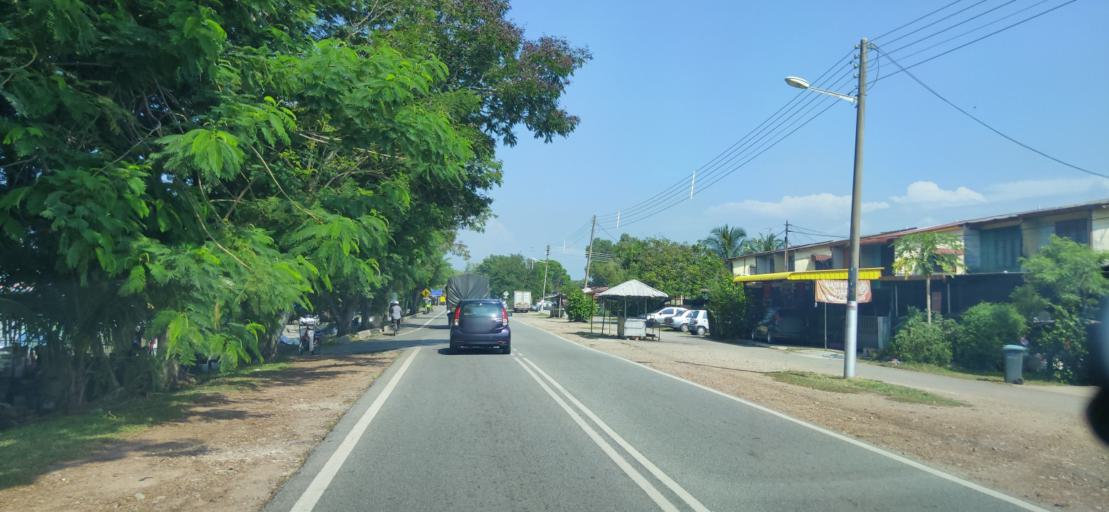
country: MY
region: Kedah
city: Sungai Petani
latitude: 5.6591
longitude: 100.4823
